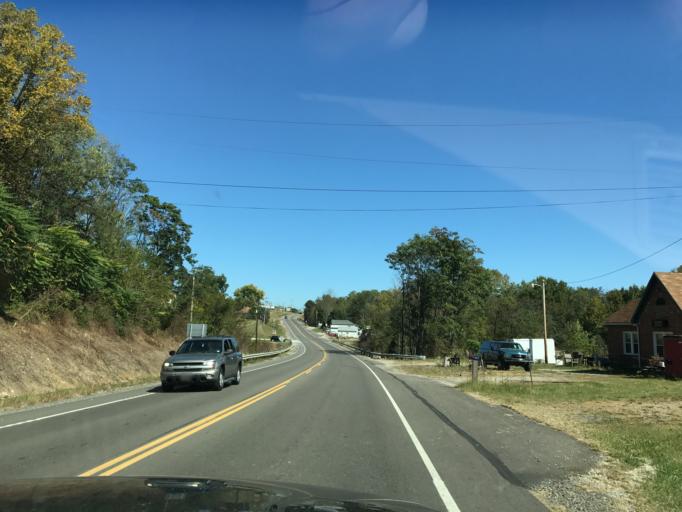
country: US
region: Ohio
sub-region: Muskingum County
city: Pleasant Grove
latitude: 39.9500
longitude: -81.9460
